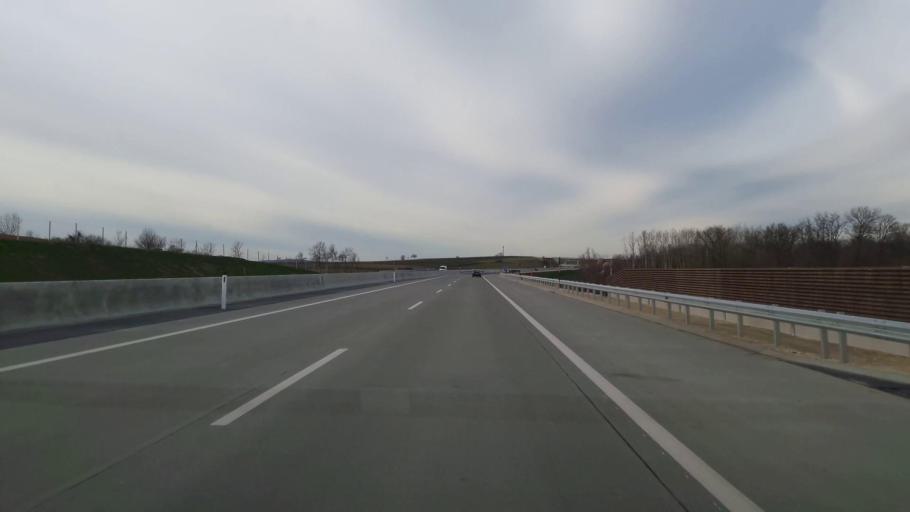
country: AT
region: Lower Austria
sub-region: Politischer Bezirk Mistelbach
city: Herrnbaumgarten
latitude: 48.6664
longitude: 16.6807
